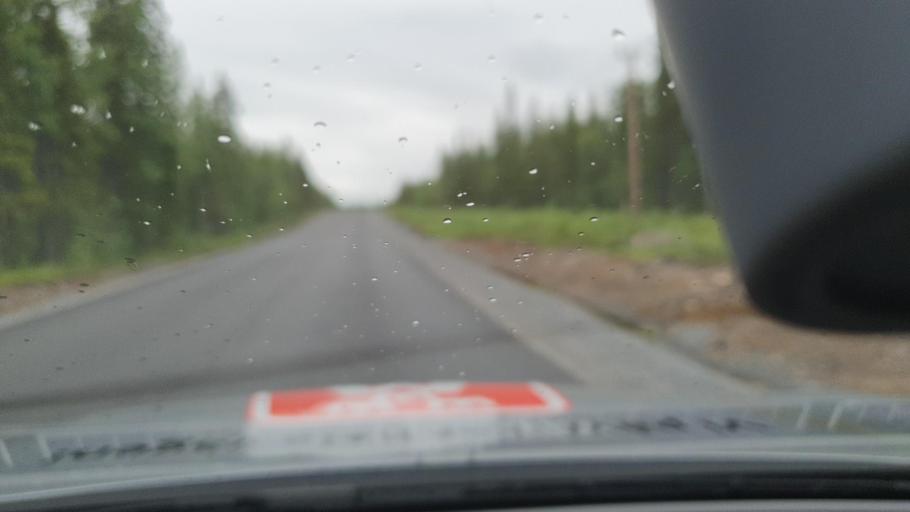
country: SE
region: Norrbotten
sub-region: Overkalix Kommun
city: OEverkalix
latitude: 66.6641
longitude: 23.2180
